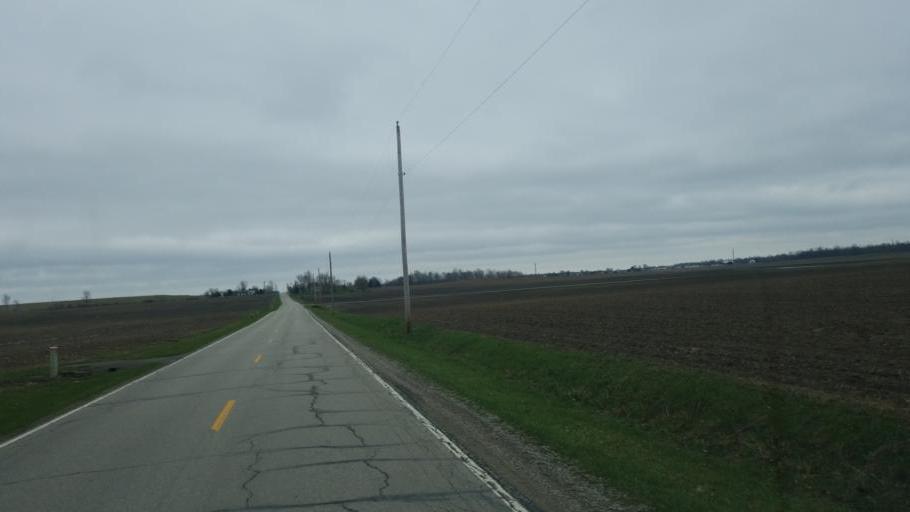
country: US
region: Ohio
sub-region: Crawford County
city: Bucyrus
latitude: 40.8509
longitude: -82.9402
